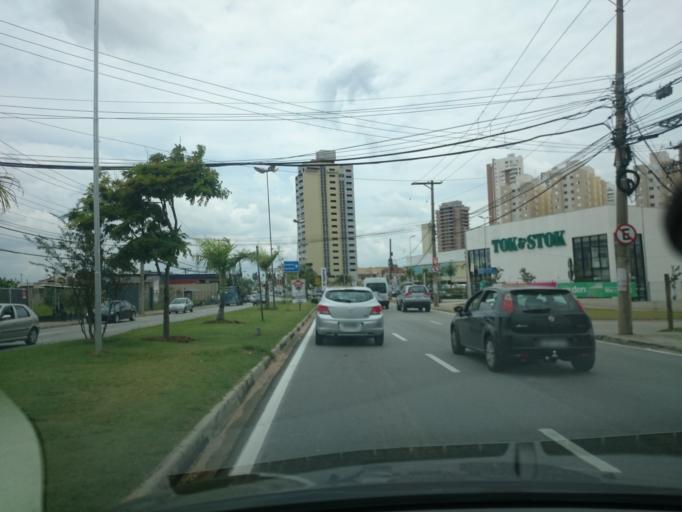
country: BR
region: Sao Paulo
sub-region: Votorantim
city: Votorantim
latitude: -23.5365
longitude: -47.4657
